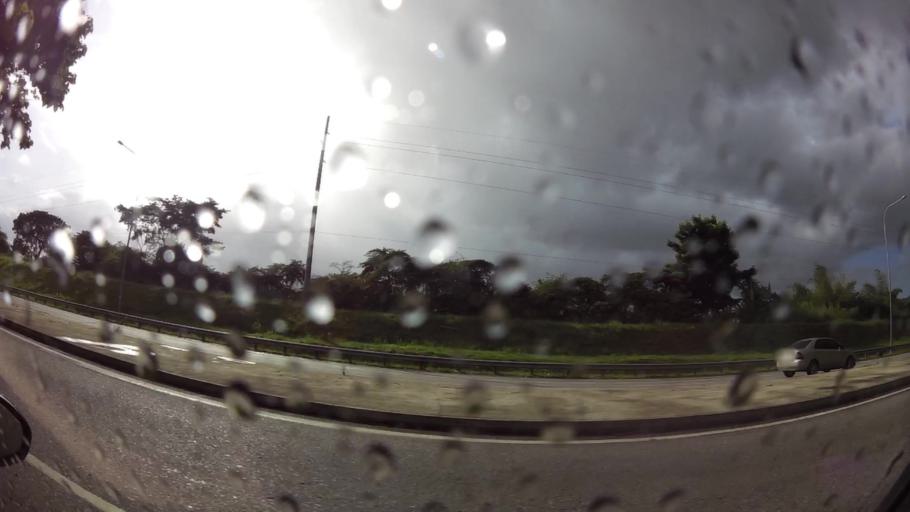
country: TT
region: Tunapuna/Piarco
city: Tunapuna
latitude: 10.6392
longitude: -61.4313
